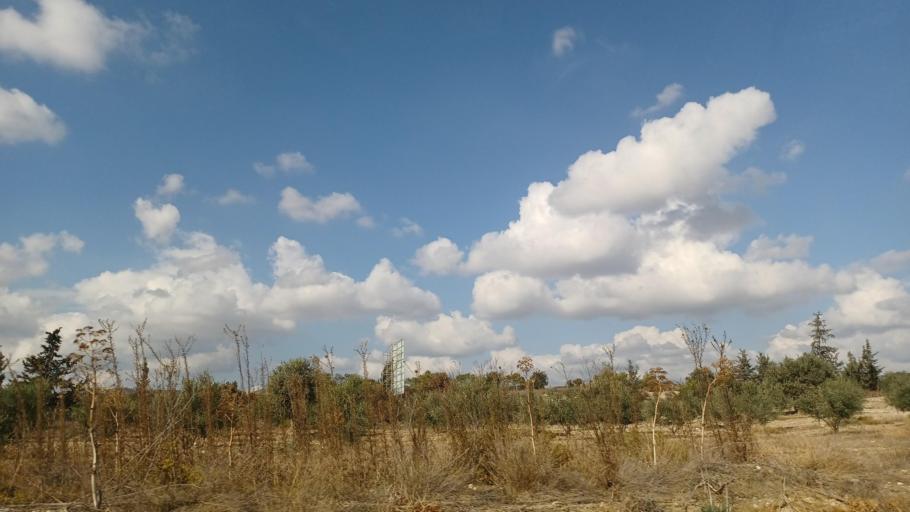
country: CY
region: Limassol
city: Pyrgos
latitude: 34.7311
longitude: 33.2818
